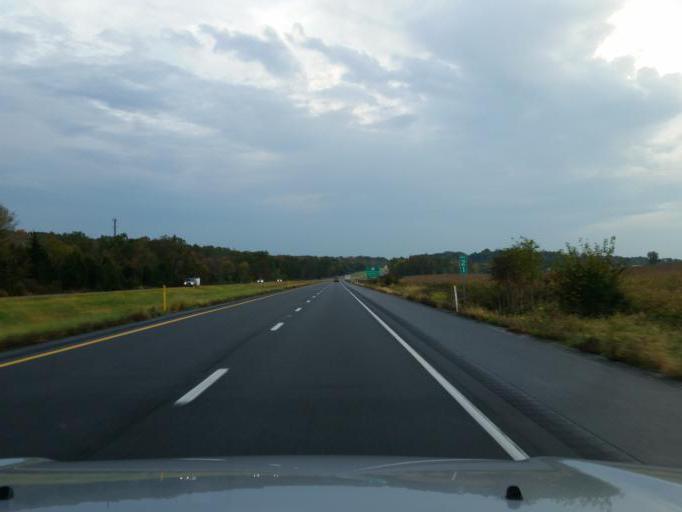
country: US
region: Pennsylvania
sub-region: Adams County
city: Lake Meade
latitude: 39.9681
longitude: -77.1289
